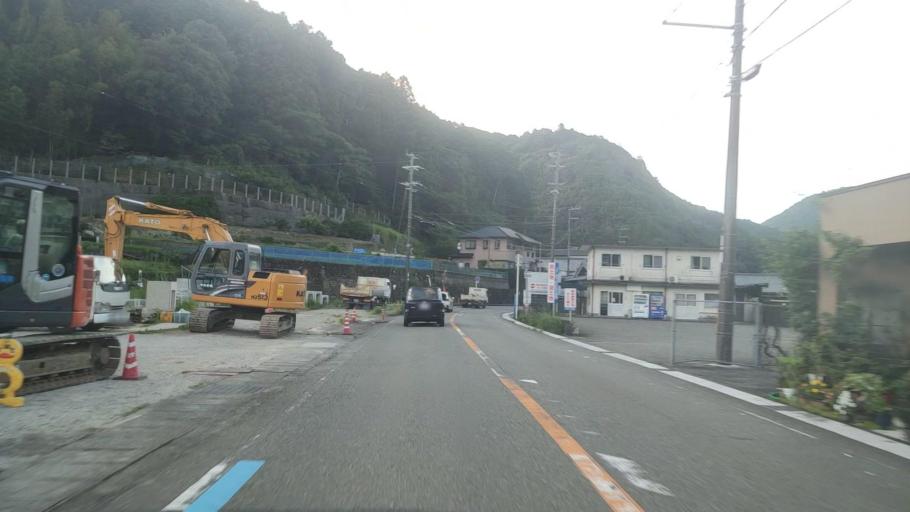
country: JP
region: Wakayama
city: Tanabe
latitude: 33.7944
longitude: 135.5186
